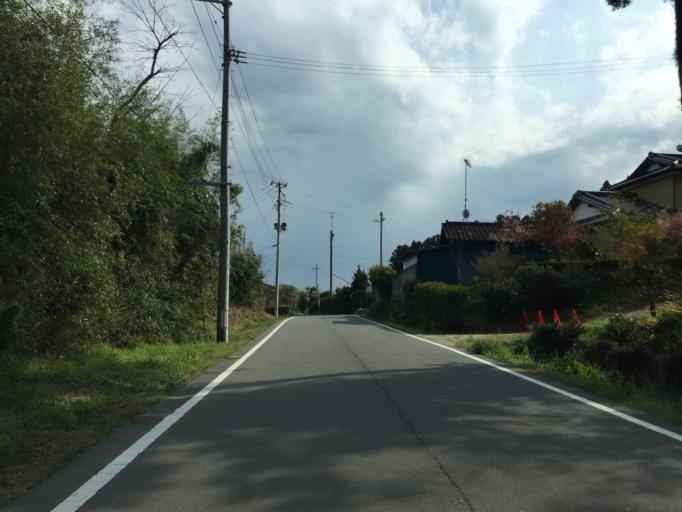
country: JP
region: Fukushima
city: Iwaki
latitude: 37.1261
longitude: 140.9027
